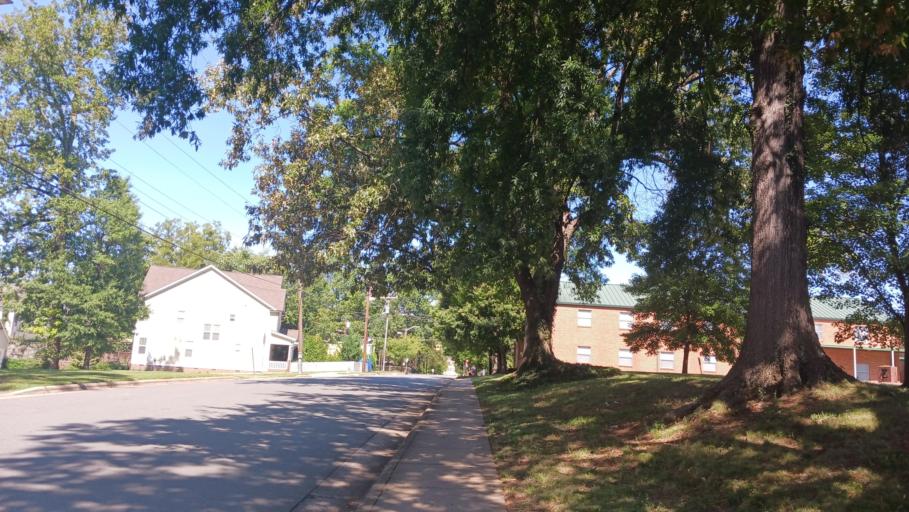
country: US
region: North Carolina
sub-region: Mecklenburg County
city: Charlotte
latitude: 35.2084
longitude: -80.8343
